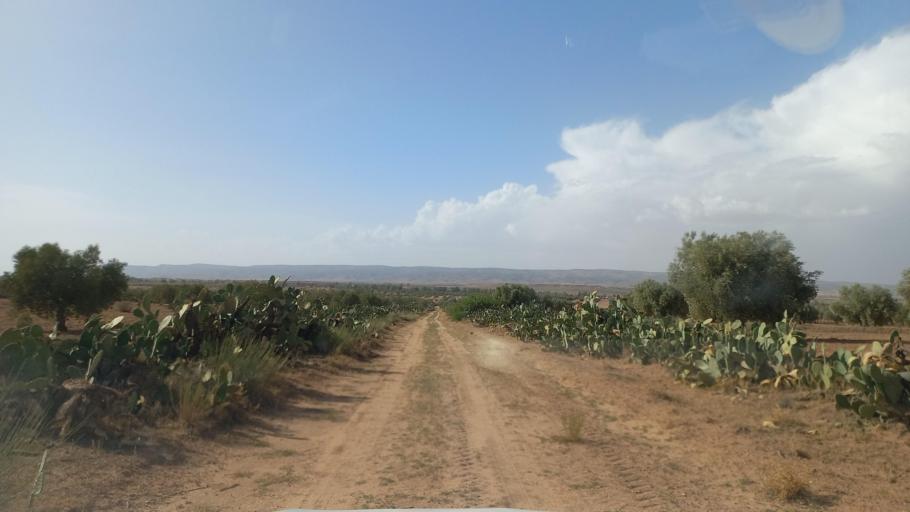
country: TN
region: Al Qasrayn
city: Kasserine
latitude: 35.2136
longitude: 8.9512
